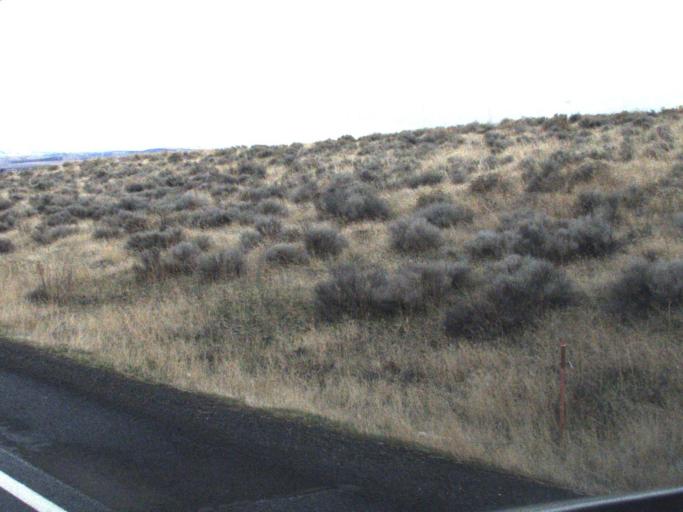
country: US
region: Washington
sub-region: Walla Walla County
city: Burbank
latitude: 46.0571
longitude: -118.7248
